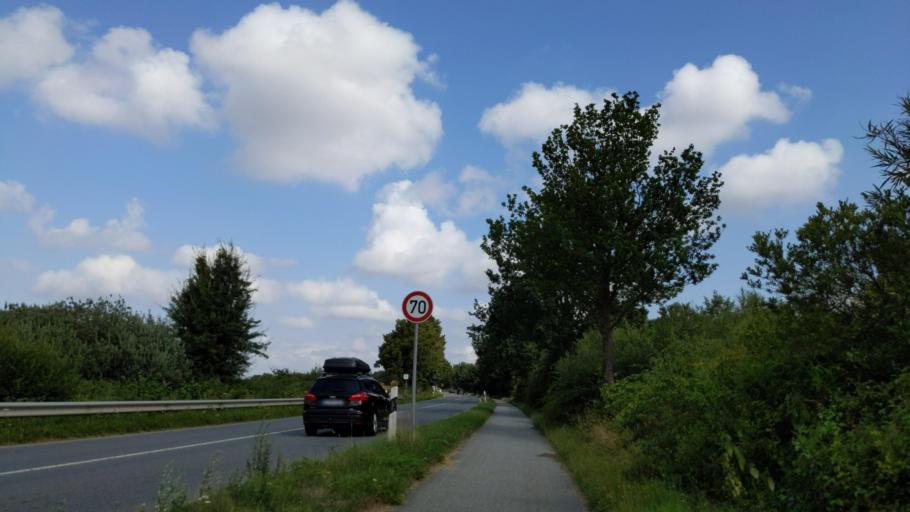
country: DE
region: Schleswig-Holstein
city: Stockelsdorf
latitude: 53.9209
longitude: 10.6396
